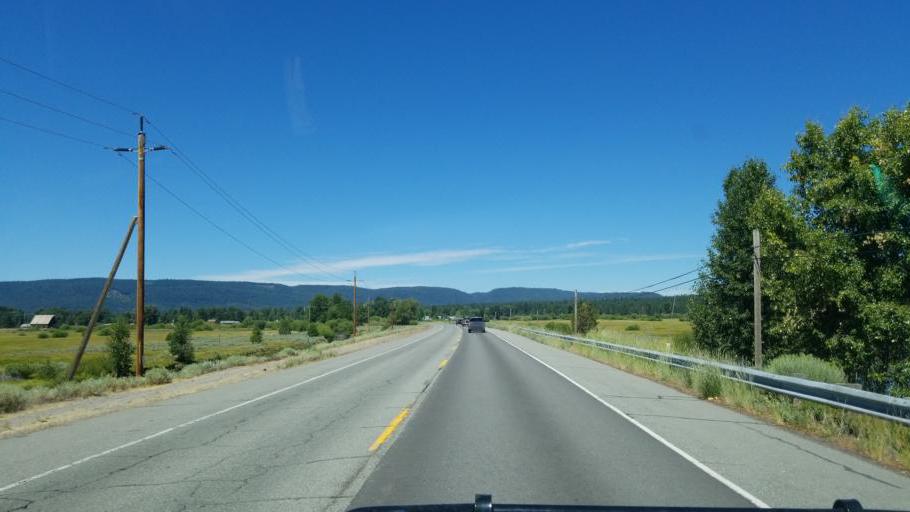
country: US
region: California
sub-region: Plumas County
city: Chester
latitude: 40.3131
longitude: -121.2110
